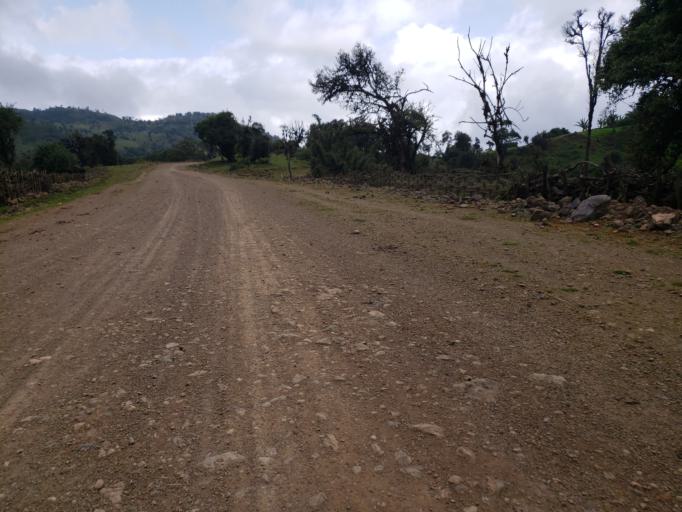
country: ET
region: Oromiya
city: Dodola
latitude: 6.7089
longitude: 39.3736
